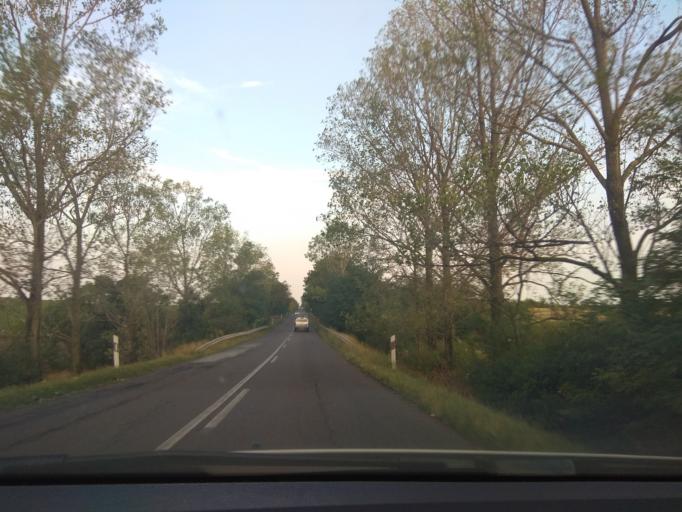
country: HU
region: Heves
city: Andornaktalya
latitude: 47.8313
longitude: 20.4474
